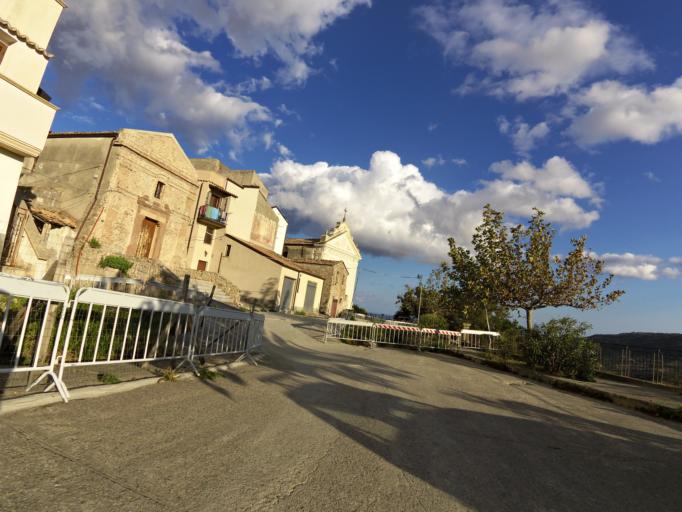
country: IT
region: Calabria
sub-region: Provincia di Reggio Calabria
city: Caulonia
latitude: 38.3795
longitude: 16.4084
